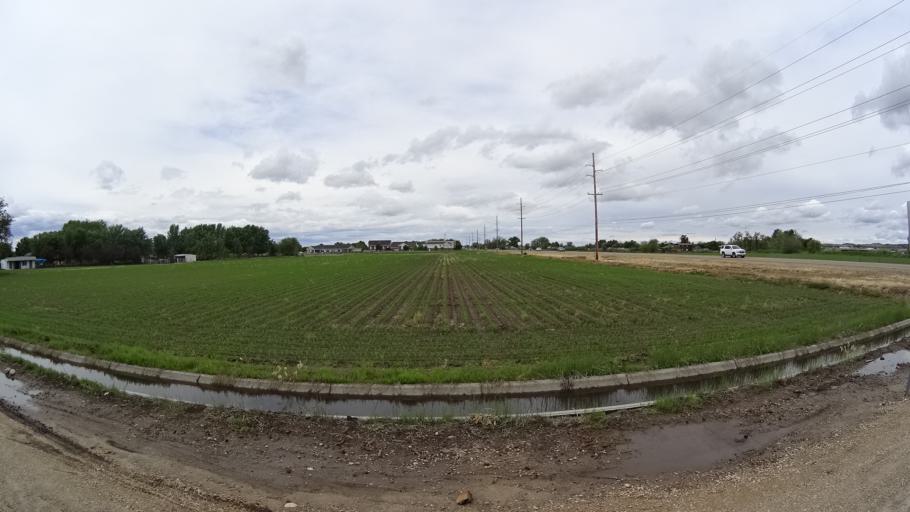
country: US
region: Idaho
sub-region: Ada County
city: Star
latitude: 43.6913
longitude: -116.4433
